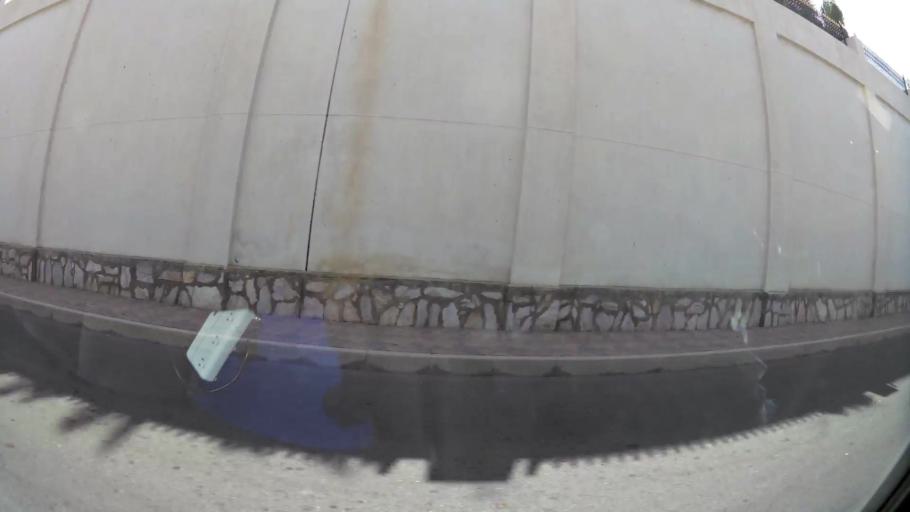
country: OM
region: Muhafazat Masqat
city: Bawshar
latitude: 23.5955
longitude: 58.4513
